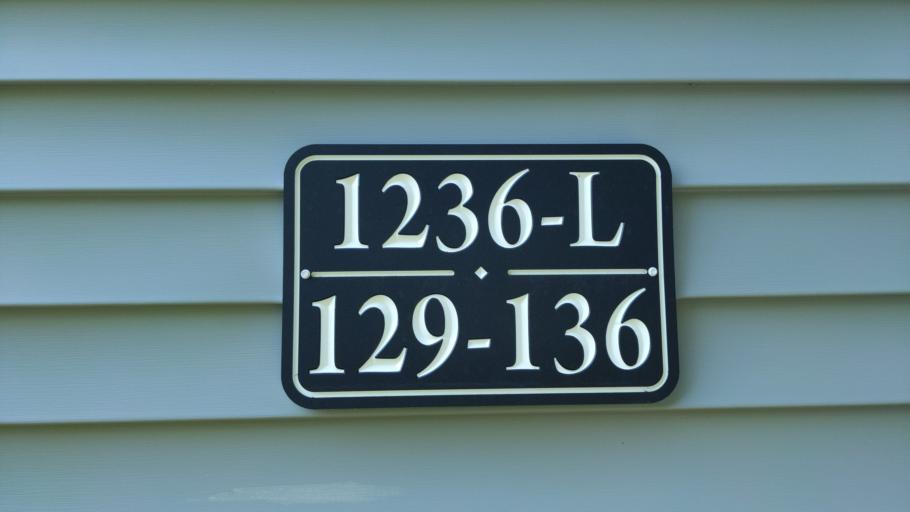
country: US
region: Virginia
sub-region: Montgomery County
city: Blacksburg
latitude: 37.2416
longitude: -80.4321
